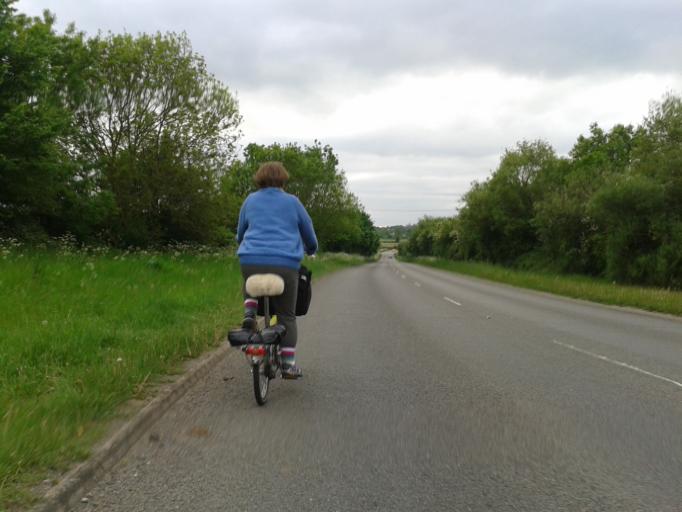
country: GB
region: England
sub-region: Leicestershire
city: Croft
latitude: 52.5388
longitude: -1.2420
